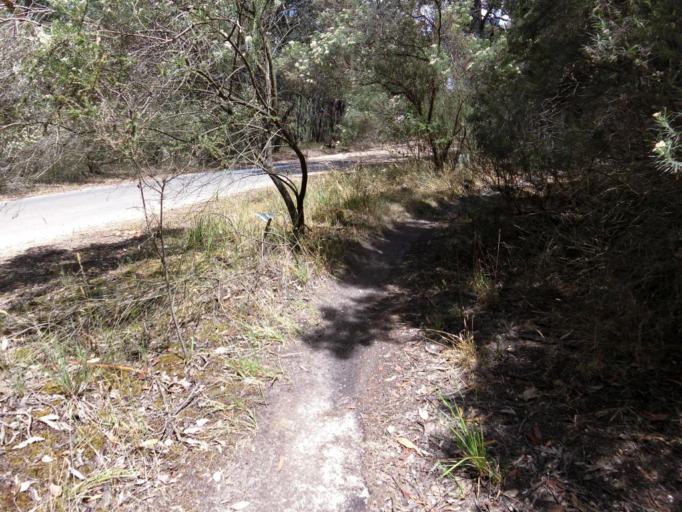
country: AU
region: Victoria
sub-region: Melton
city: Melton West
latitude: -37.4924
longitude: 144.5482
